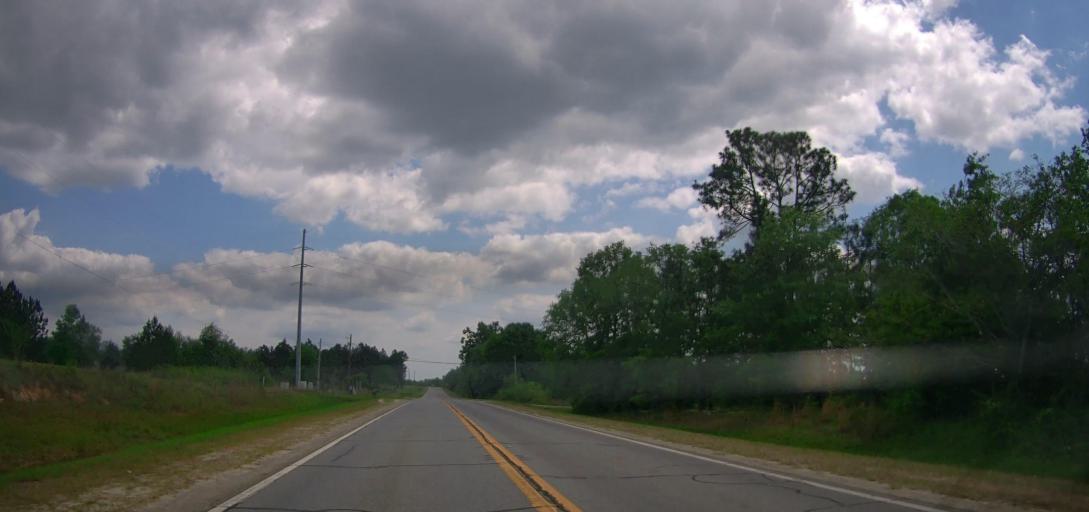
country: US
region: Georgia
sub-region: Laurens County
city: East Dublin
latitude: 32.5106
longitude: -82.8392
